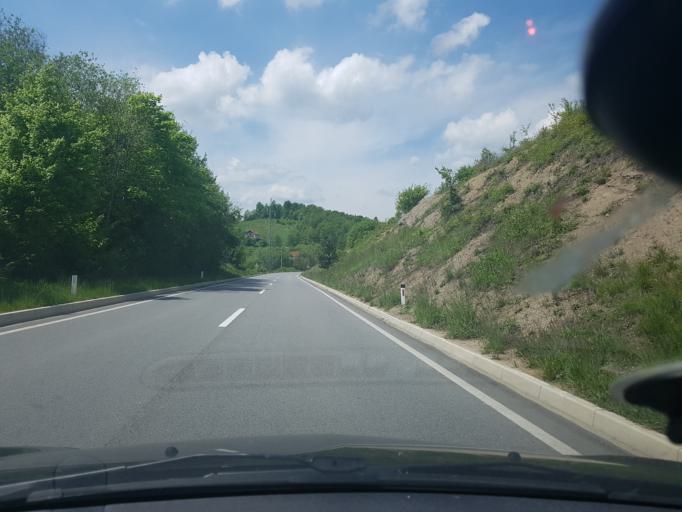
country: SI
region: Rogaska Slatina
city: Rogaska Slatina
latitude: 46.2428
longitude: 15.6581
